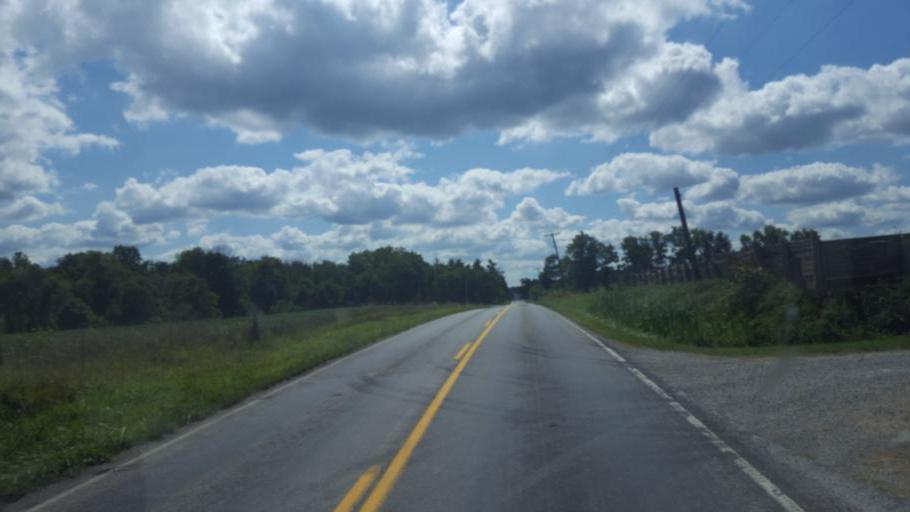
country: US
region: Ohio
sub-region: Ashland County
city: Ashland
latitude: 40.9615
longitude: -82.2820
